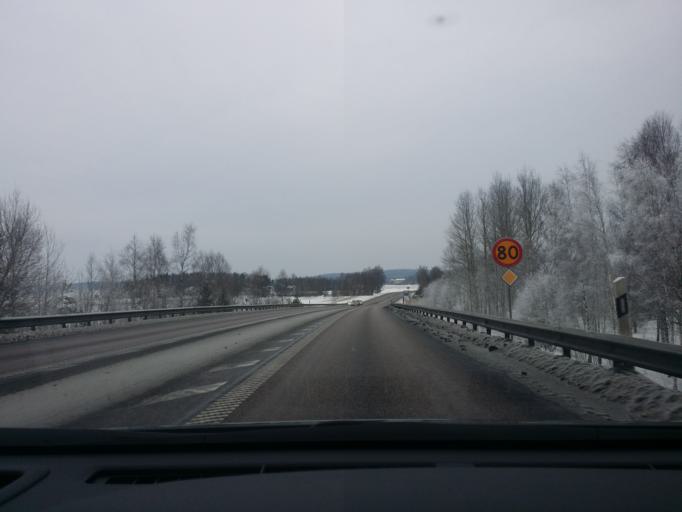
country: SE
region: Vaestra Goetaland
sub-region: Gullspangs Kommun
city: Hova
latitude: 58.8501
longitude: 14.1999
